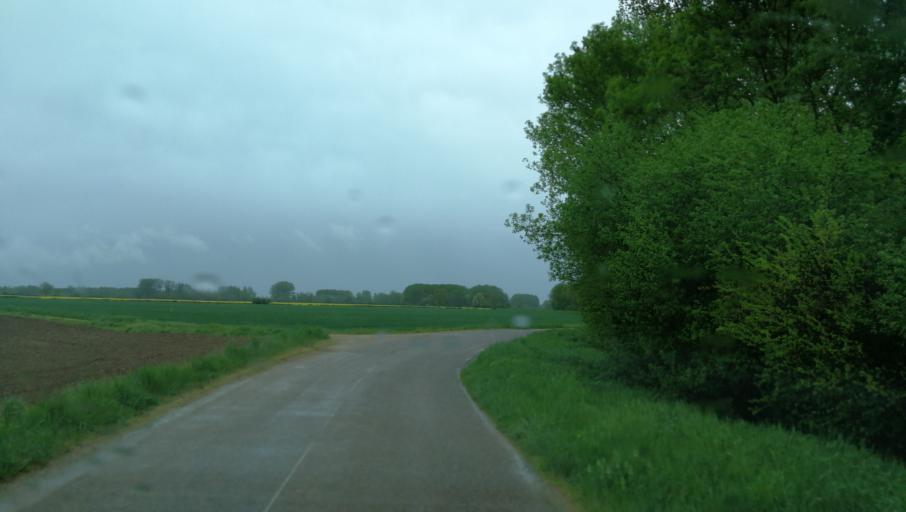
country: FR
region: Bourgogne
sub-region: Departement de Saone-et-Loire
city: Pierre-de-Bresse
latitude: 46.9337
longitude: 5.2334
